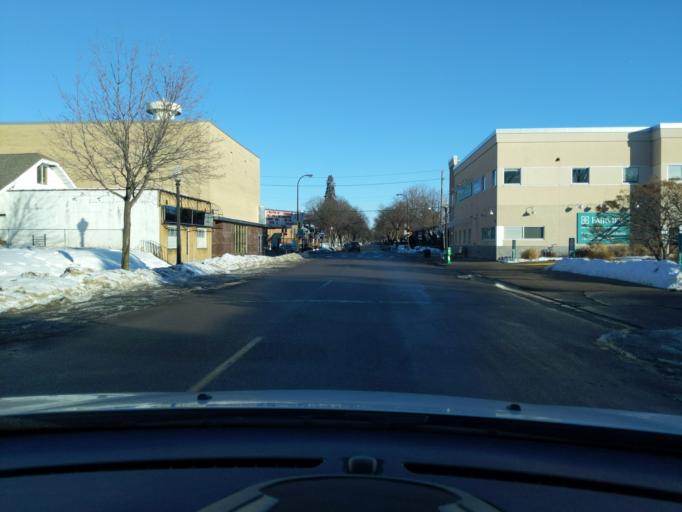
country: US
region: Minnesota
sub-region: Ramsey County
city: Lauderdale
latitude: 44.9337
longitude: -93.2127
